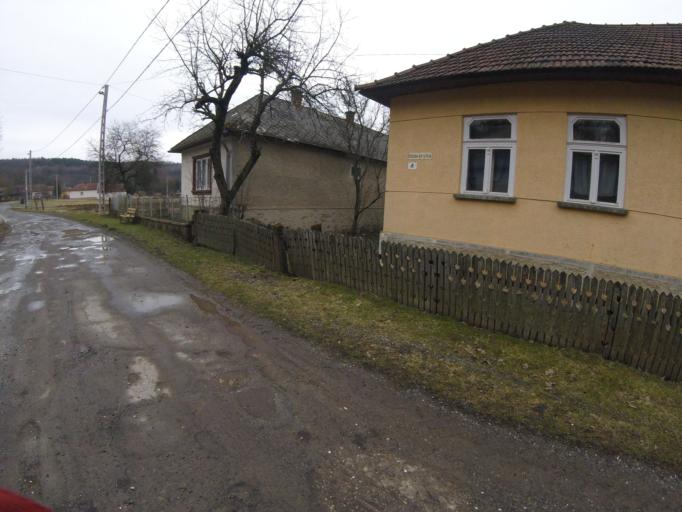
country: HU
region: Borsod-Abauj-Zemplen
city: Rudabanya
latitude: 48.4631
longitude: 20.6152
